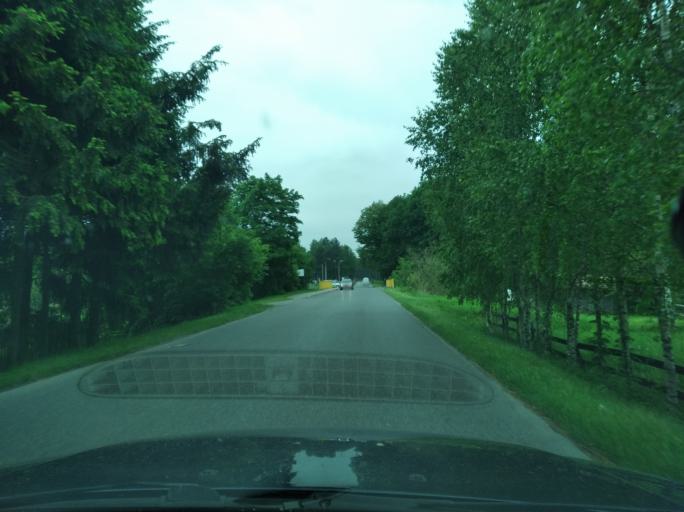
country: PL
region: Subcarpathian Voivodeship
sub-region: Powiat ropczycko-sedziszowski
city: Sedziszow Malopolski
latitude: 50.1350
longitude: 21.6691
